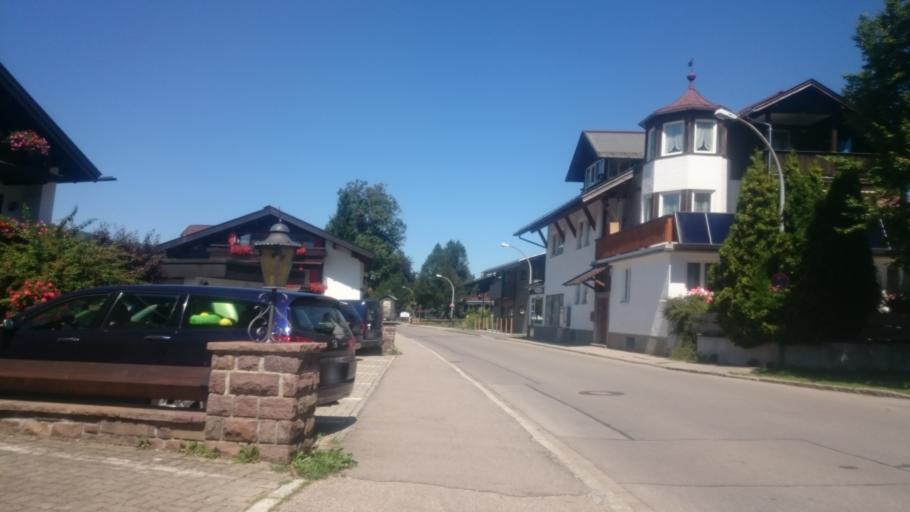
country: DE
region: Bavaria
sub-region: Swabia
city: Oberstdorf
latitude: 47.4003
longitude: 10.2794
